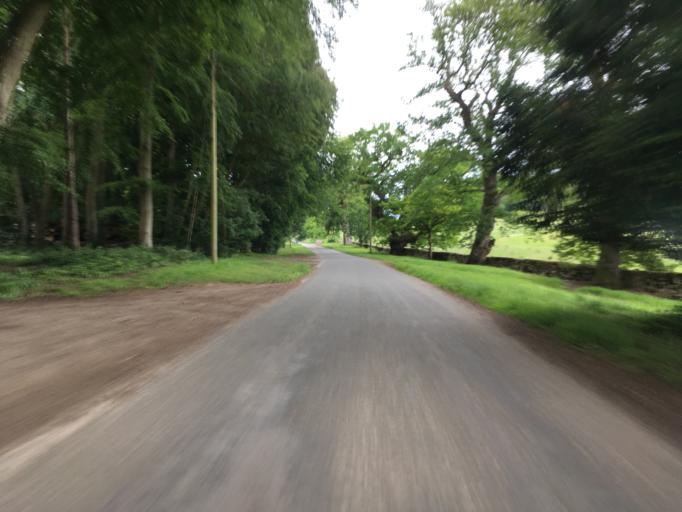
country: GB
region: England
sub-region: Wiltshire
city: Luckington
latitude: 51.5724
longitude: -2.2763
